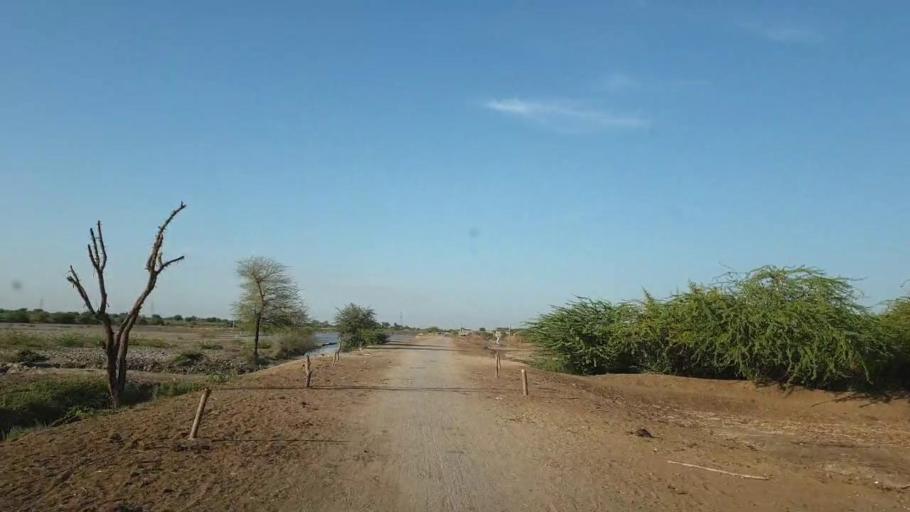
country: PK
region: Sindh
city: Kunri
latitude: 25.0951
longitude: 69.4204
